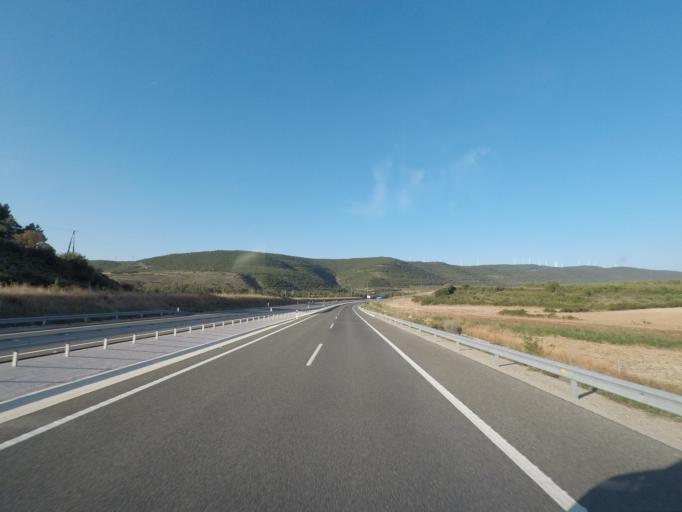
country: ES
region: Navarre
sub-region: Provincia de Navarra
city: Liedena
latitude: 42.6208
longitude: -1.2815
